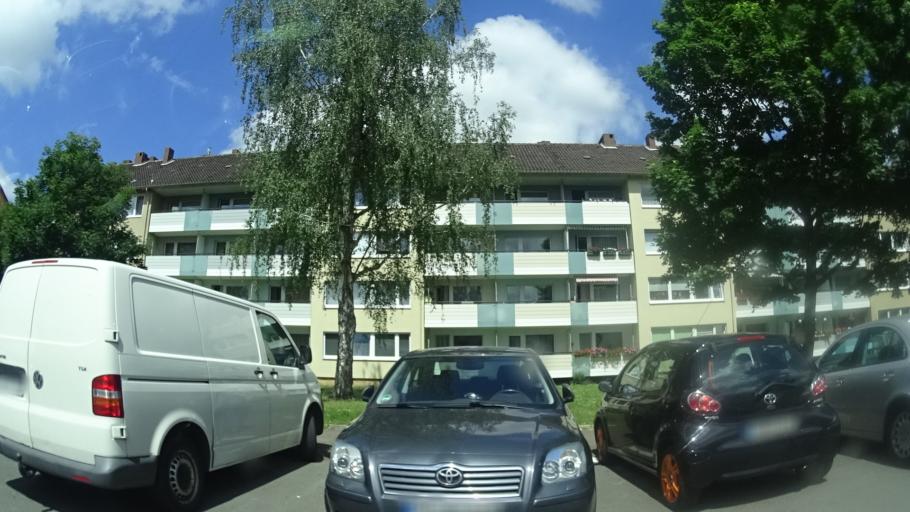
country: DE
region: Lower Saxony
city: Hildesheim
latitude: 52.1733
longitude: 9.9732
